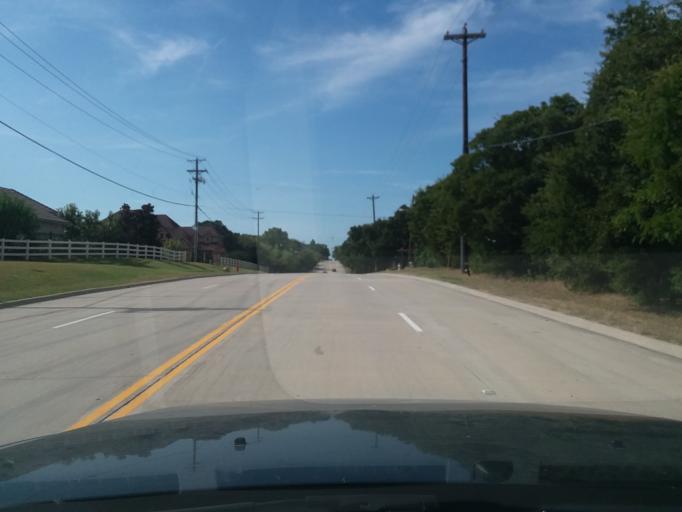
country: US
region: Texas
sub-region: Denton County
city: Flower Mound
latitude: 33.0170
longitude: -97.0885
